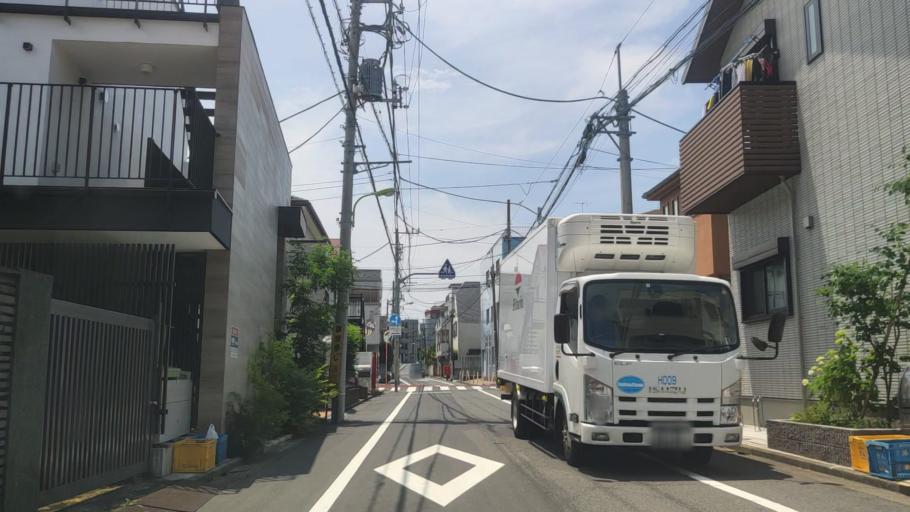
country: JP
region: Tokyo
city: Tokyo
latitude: 35.6523
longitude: 139.6653
